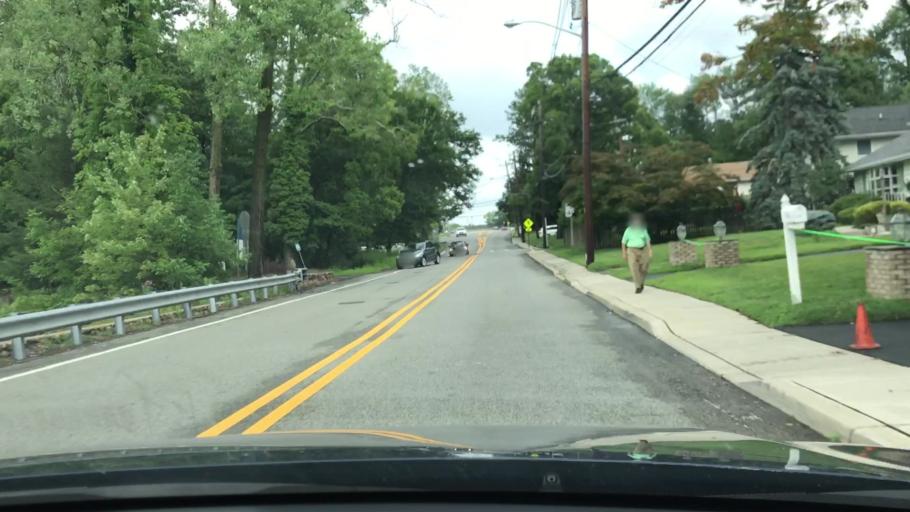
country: US
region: New Jersey
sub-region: Bergen County
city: Ramsey
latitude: 41.0594
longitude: -74.1275
